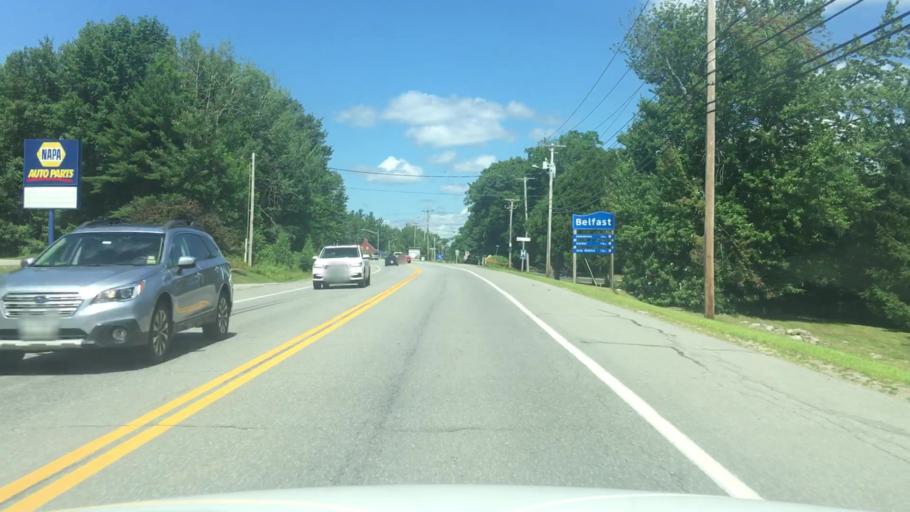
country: US
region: Maine
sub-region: Waldo County
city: Belfast
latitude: 44.4060
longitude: -68.9911
